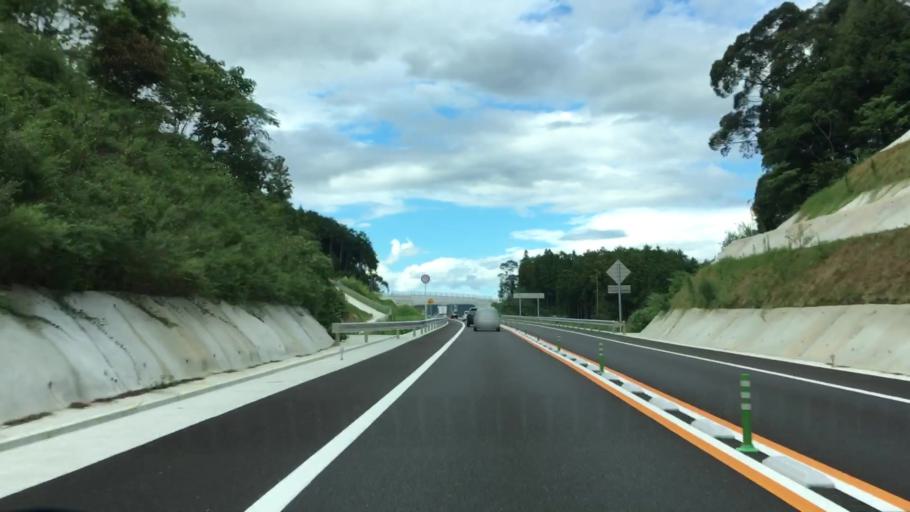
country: JP
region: Saga Prefecture
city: Imaricho-ko
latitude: 33.3289
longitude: 129.9278
